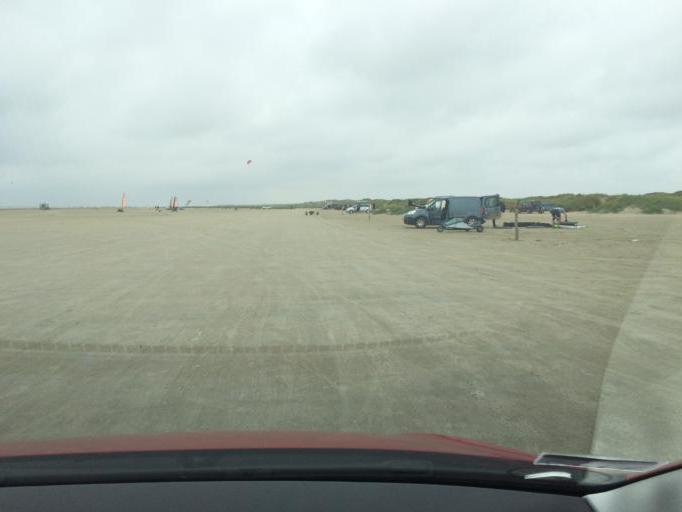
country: DK
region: South Denmark
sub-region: Fano Kommune
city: Nordby
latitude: 55.3997
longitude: 8.3929
